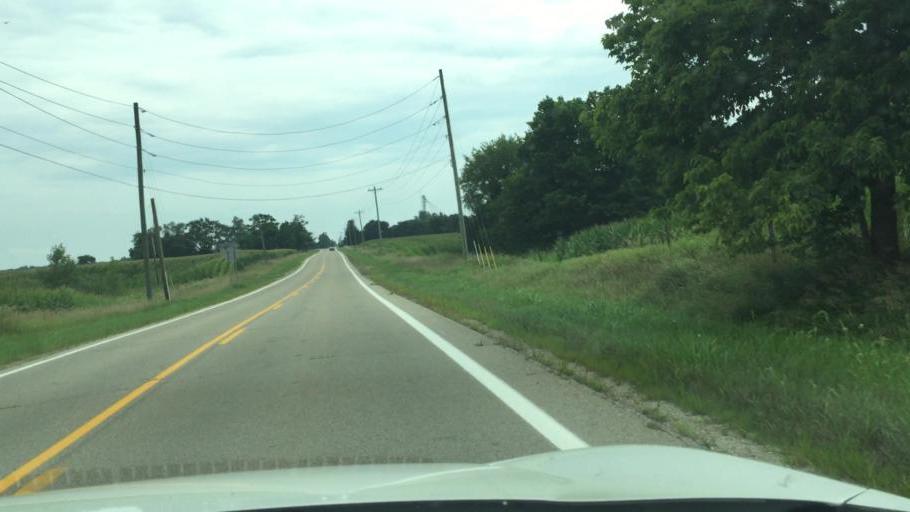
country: US
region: Ohio
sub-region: Champaign County
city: Mechanicsburg
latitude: 40.1409
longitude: -83.5299
